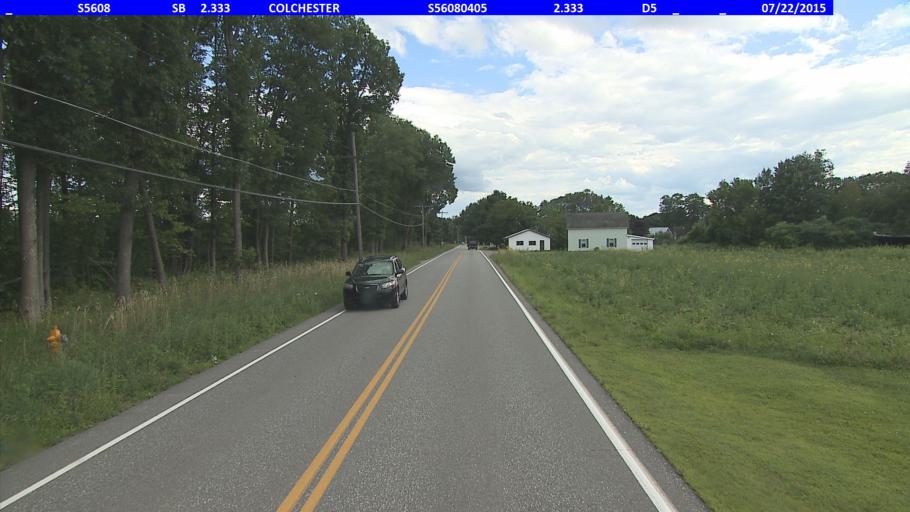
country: US
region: Vermont
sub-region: Chittenden County
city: Winooski
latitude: 44.5304
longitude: -73.2076
